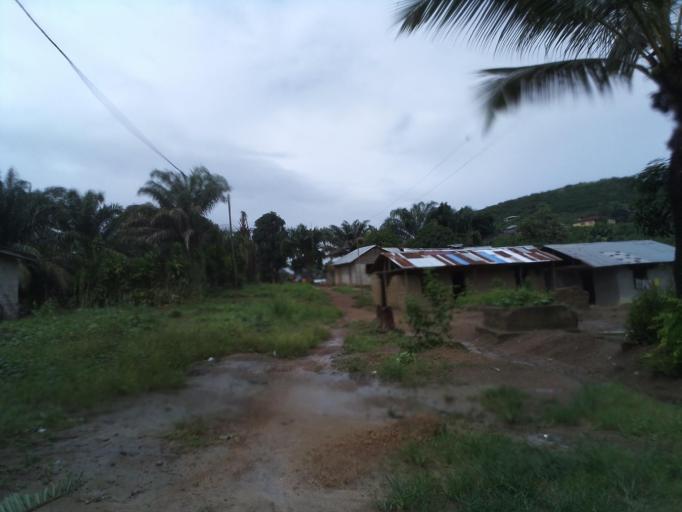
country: SL
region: Eastern Province
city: Kenema
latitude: 7.8509
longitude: -11.1962
